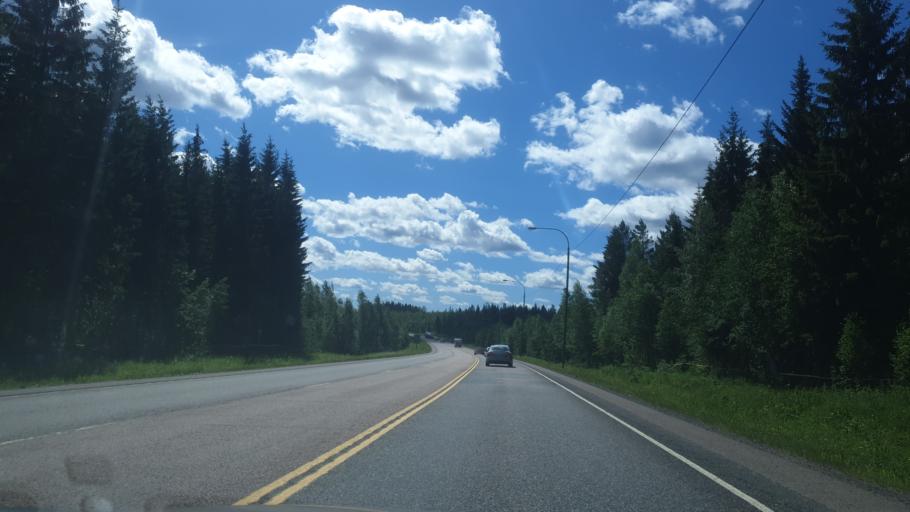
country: FI
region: Northern Savo
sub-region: Varkaus
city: Varkaus
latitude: 62.3881
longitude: 27.8113
